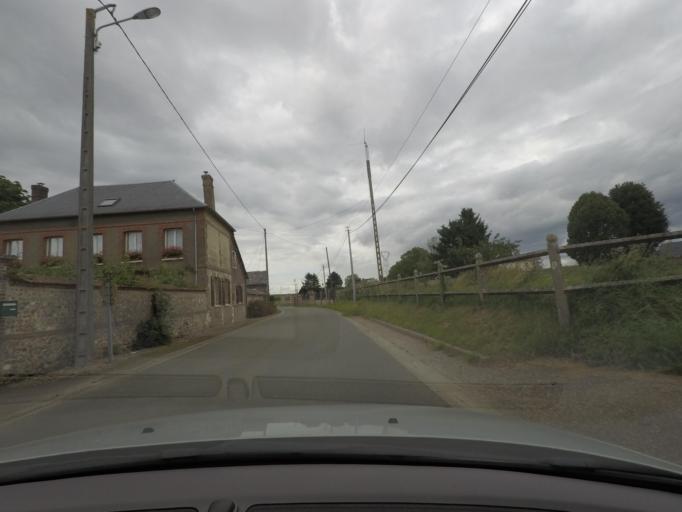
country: FR
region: Haute-Normandie
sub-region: Departement de l'Eure
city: Fleury-sur-Andelle
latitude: 49.2897
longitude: 1.3385
